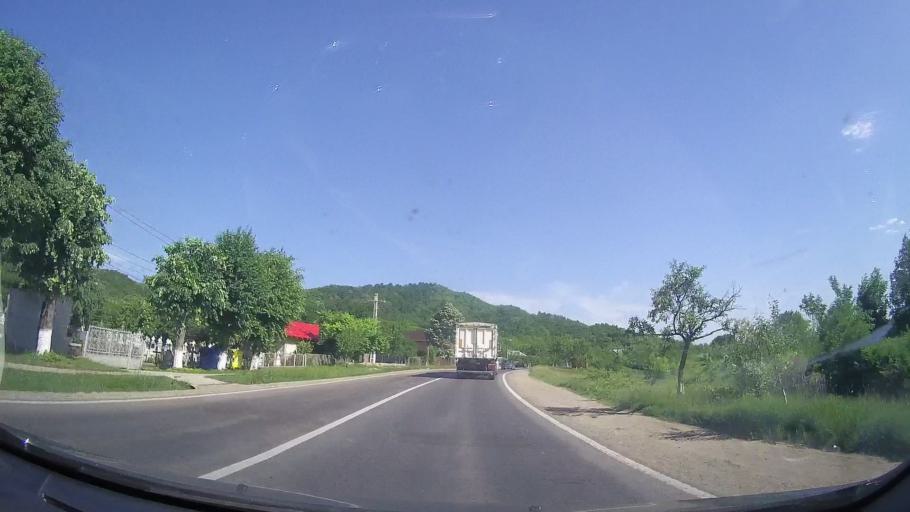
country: RO
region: Prahova
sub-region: Comuna Gura Vitioarei
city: Fagetu
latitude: 45.1296
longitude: 26.0337
